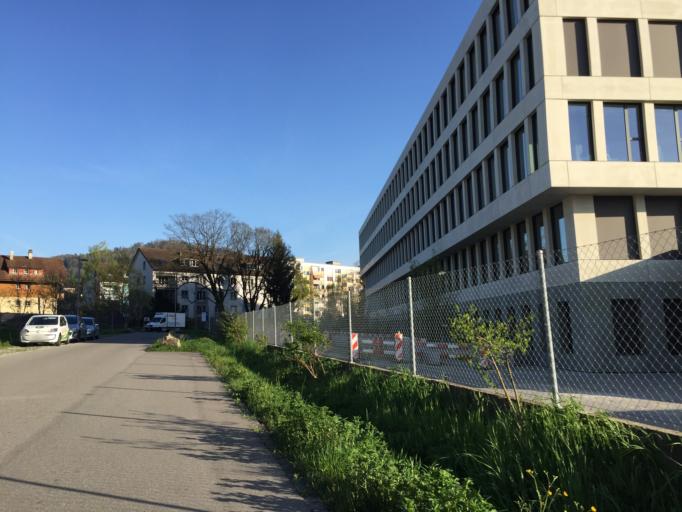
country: CH
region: Bern
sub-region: Bern-Mittelland District
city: Koniz
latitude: 46.9344
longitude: 7.4196
